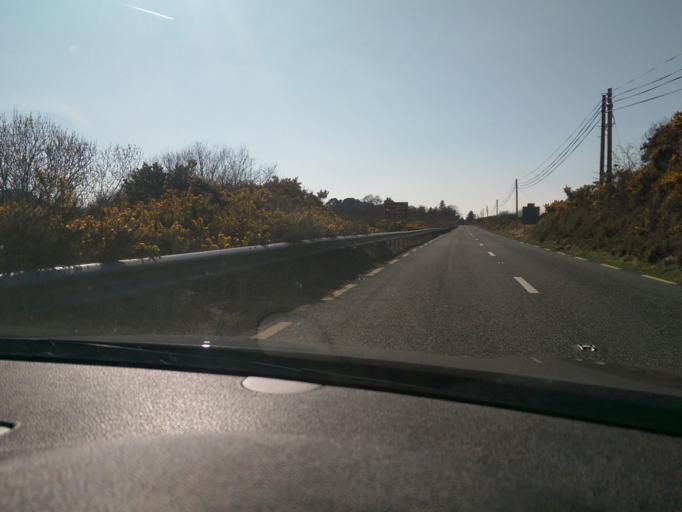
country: IE
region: Connaught
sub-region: County Galway
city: Clifden
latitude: 53.4670
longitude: -9.7457
